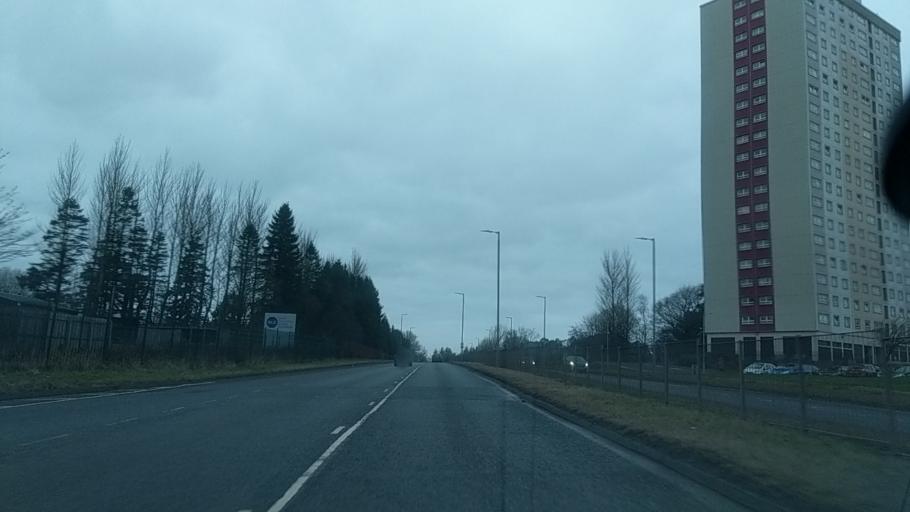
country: GB
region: Scotland
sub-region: South Lanarkshire
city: East Kilbride
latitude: 55.7543
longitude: -4.1579
